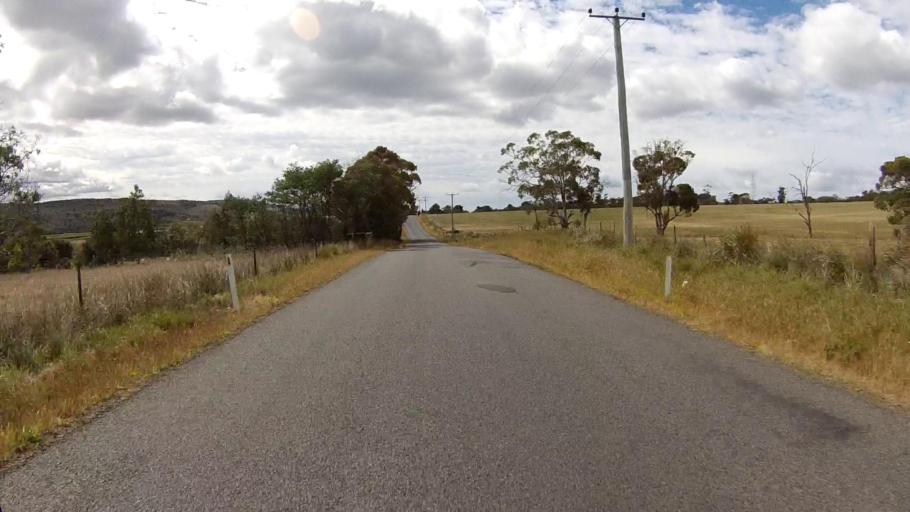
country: AU
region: Tasmania
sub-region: Clarence
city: Cambridge
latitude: -42.7683
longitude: 147.4056
